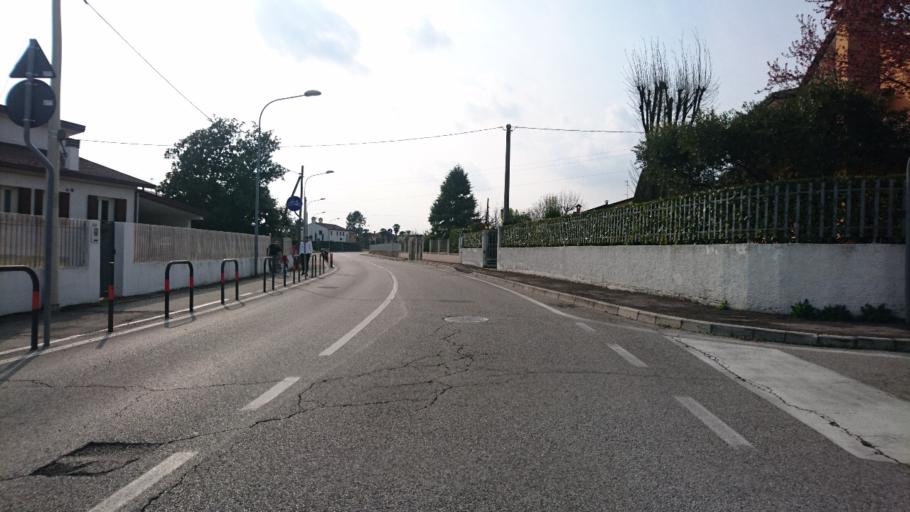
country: IT
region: Veneto
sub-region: Provincia di Padova
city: San Vito
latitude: 45.4107
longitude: 11.9697
